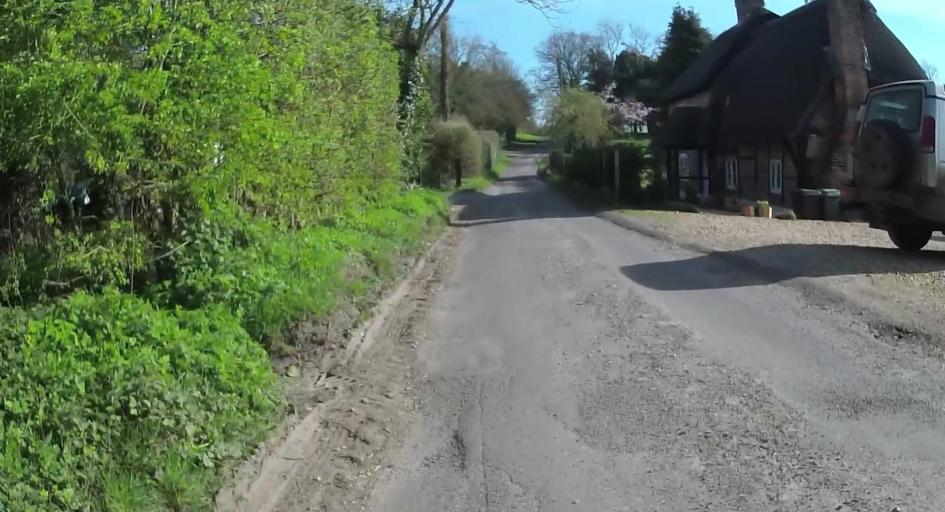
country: GB
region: England
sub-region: Hampshire
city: Highclere
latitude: 51.2702
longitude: -1.3718
